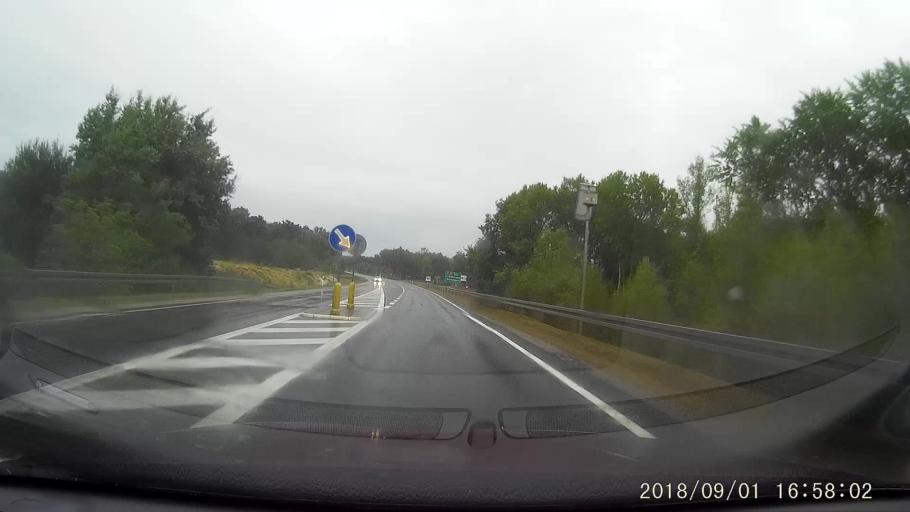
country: PL
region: Lubusz
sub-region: Powiat zielonogorski
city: Swidnica
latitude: 51.9238
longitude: 15.4181
